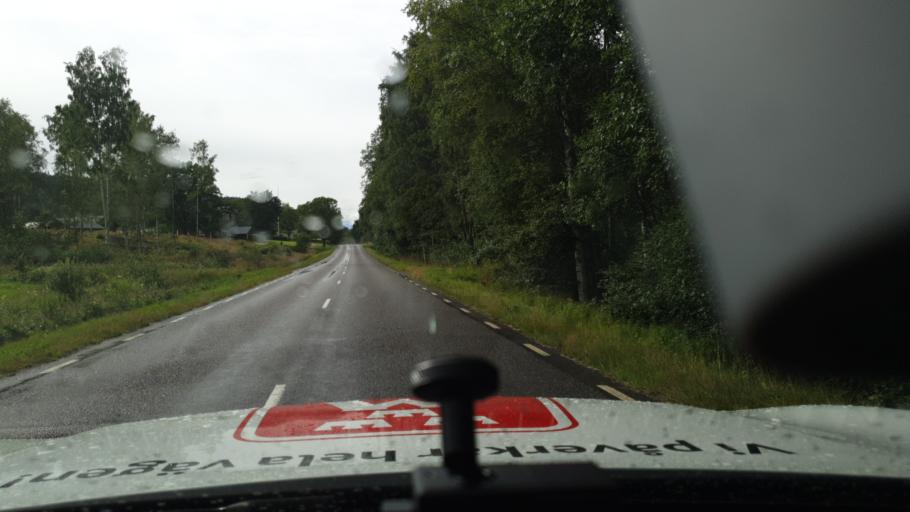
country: SE
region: Vaermland
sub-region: Sunne Kommun
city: Sunne
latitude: 59.8023
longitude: 13.0478
